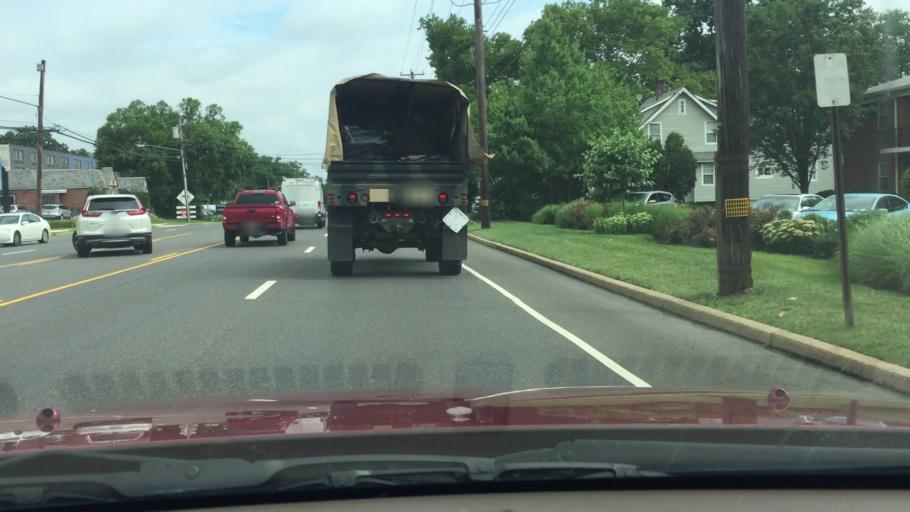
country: US
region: Pennsylvania
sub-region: Montgomery County
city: Horsham
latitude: 40.1749
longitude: -75.1280
